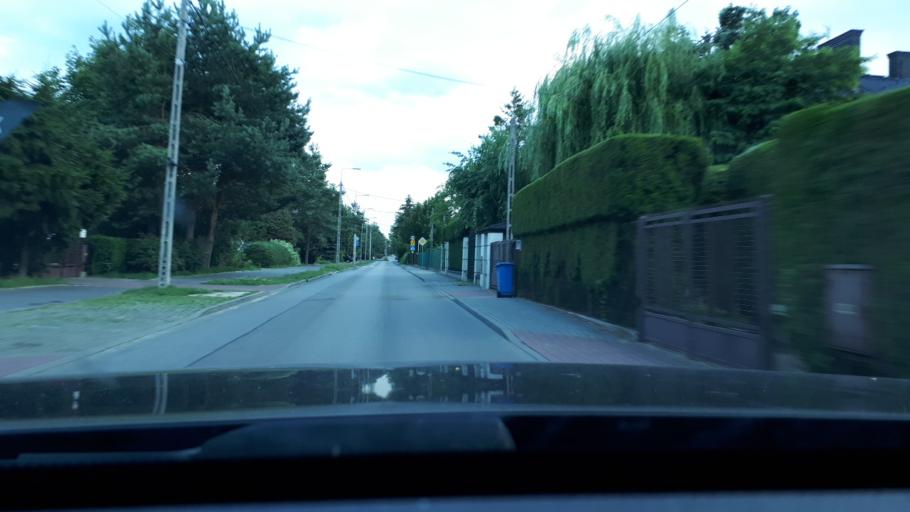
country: PL
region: Masovian Voivodeship
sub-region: Powiat pruszkowski
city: Komorow
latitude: 52.1569
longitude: 20.8237
